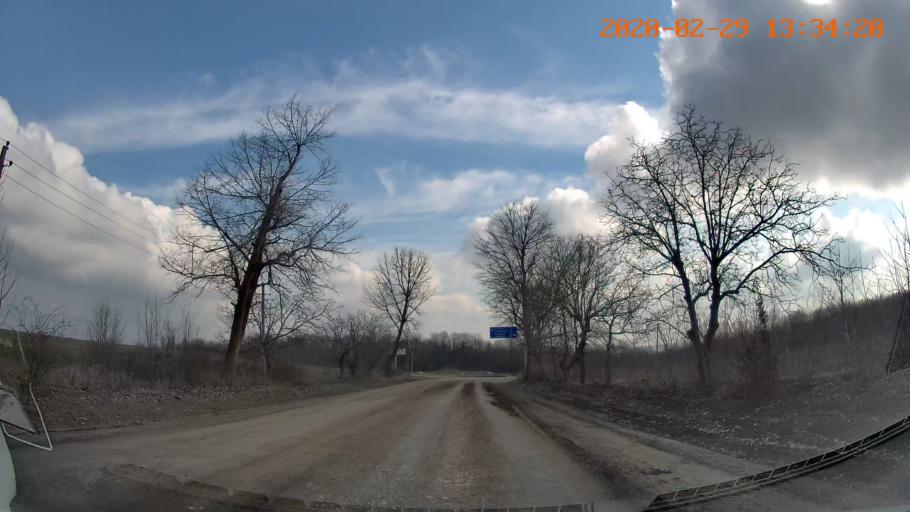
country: MD
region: Telenesti
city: Camenca
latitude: 47.8695
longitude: 28.6219
